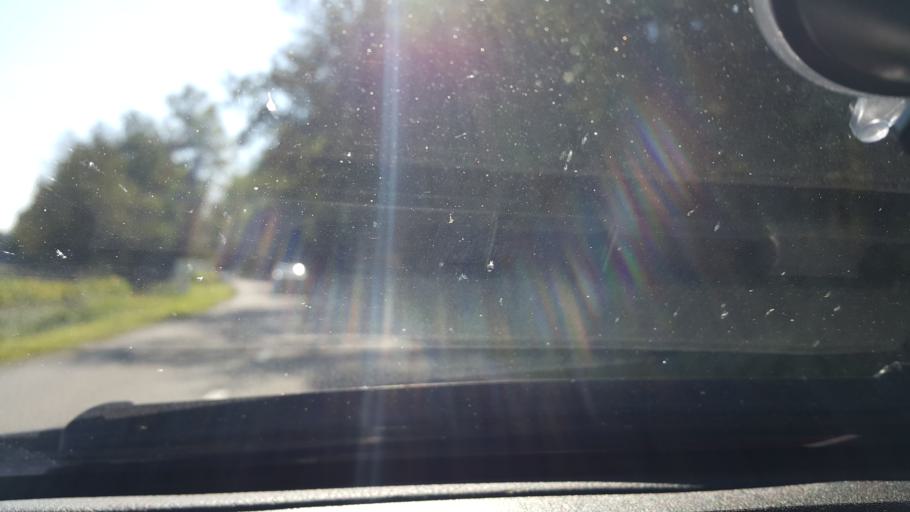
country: SI
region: Miklavz na Dravskem Polju
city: Miklavz na Dravskem Polju
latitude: 46.4750
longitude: 15.7073
